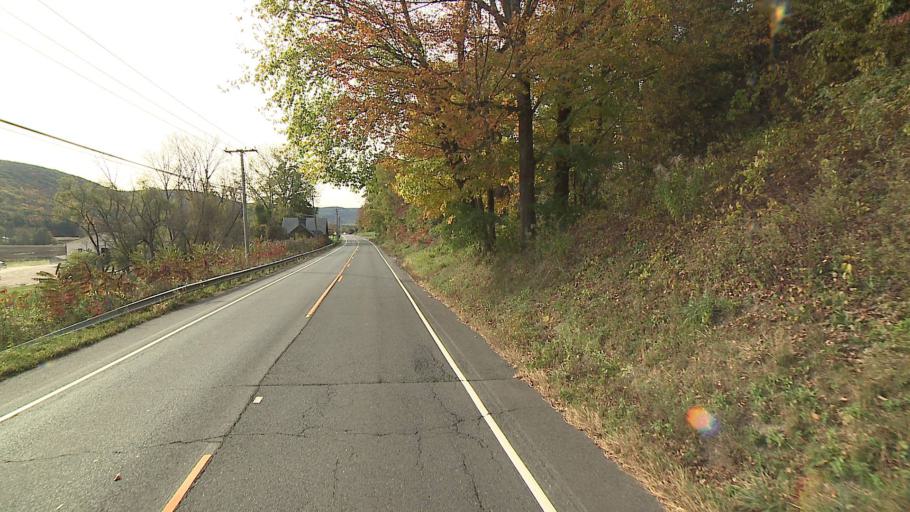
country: US
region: Connecticut
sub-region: Litchfield County
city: Canaan
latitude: 42.0061
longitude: -73.2431
